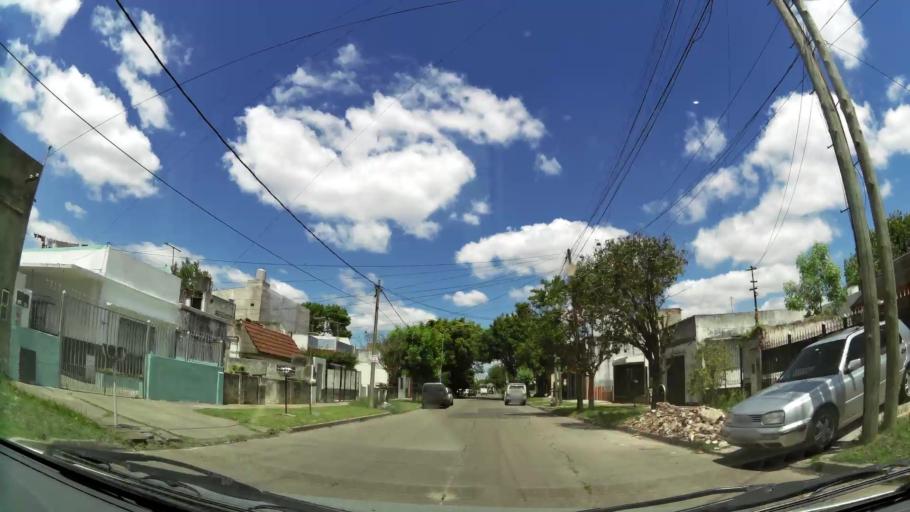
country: AR
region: Buenos Aires
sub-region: Partido de Lanus
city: Lanus
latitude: -34.7081
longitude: -58.4124
